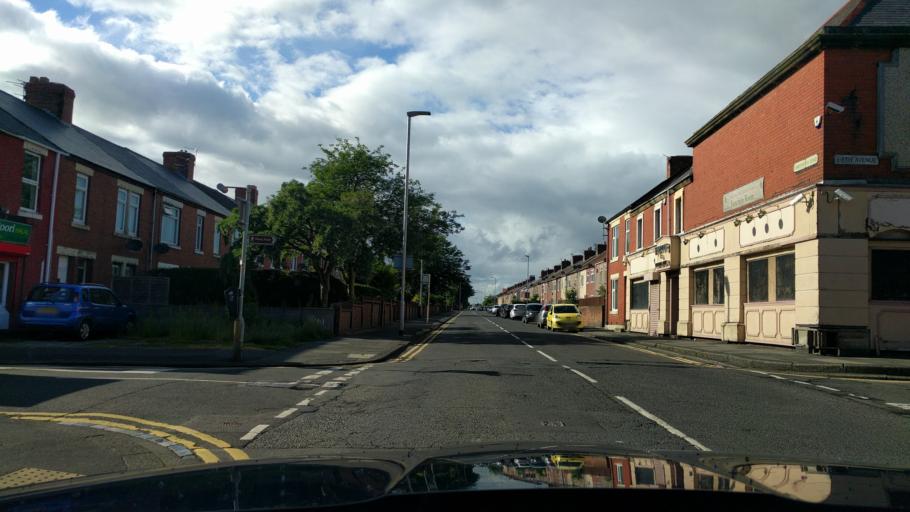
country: GB
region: England
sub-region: Northumberland
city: Ashington
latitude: 55.1770
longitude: -1.5592
